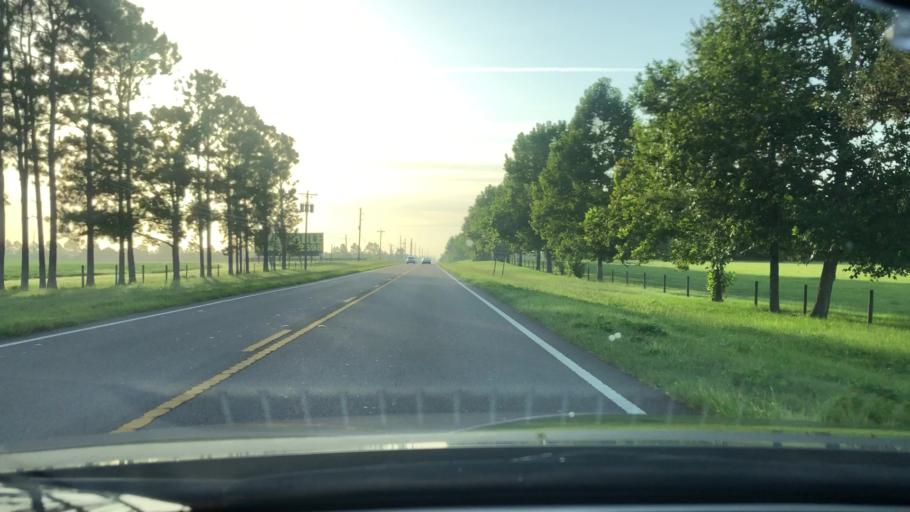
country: US
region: Florida
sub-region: Marion County
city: Belleview
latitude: 29.0261
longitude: -82.2089
